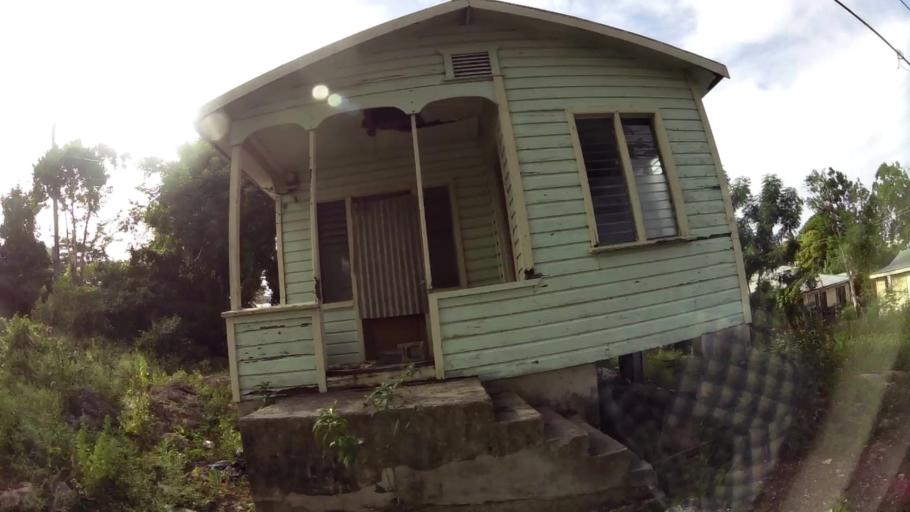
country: AG
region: Saint George
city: Piggotts
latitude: 17.1426
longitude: -61.8081
